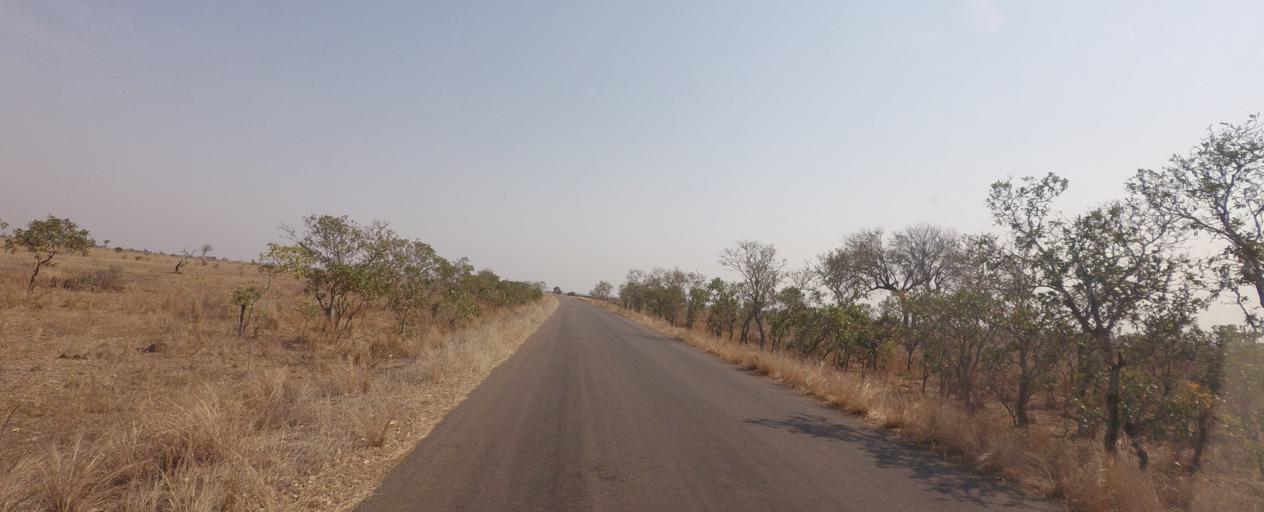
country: ZA
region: Limpopo
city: Thulamahashi
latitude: -24.3320
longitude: 31.7562
